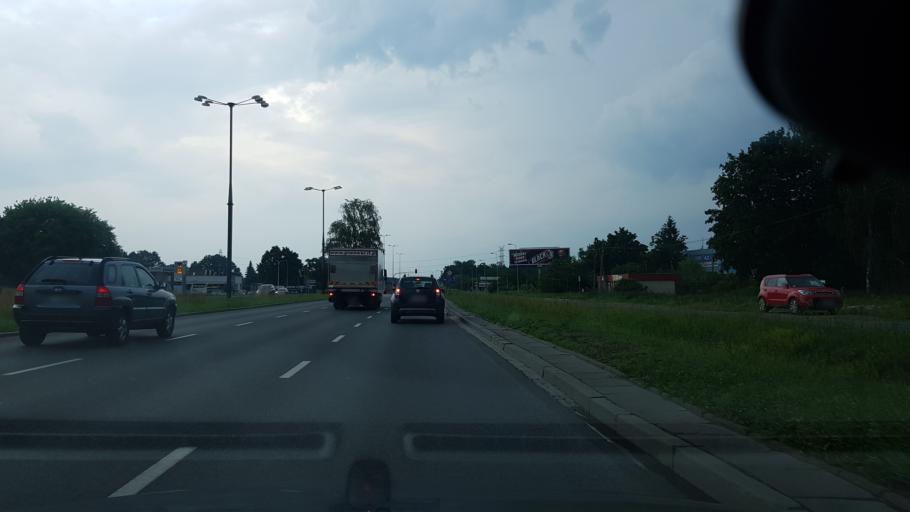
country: PL
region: Masovian Voivodeship
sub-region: Warszawa
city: Bialoleka
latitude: 52.3483
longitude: 20.9480
